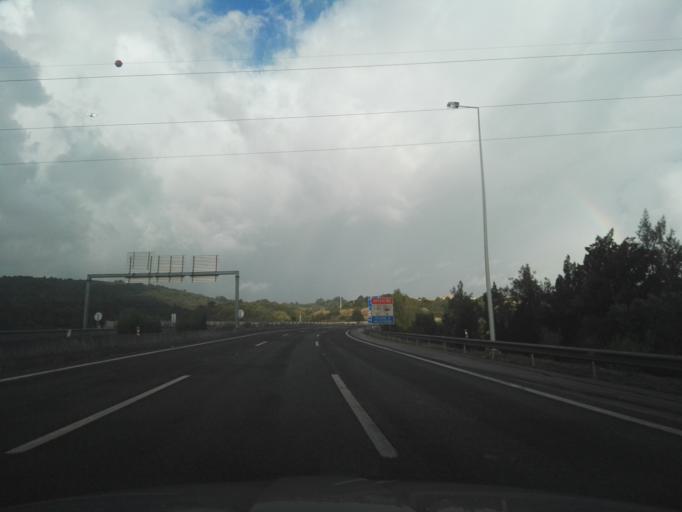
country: PT
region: Lisbon
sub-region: Vila Franca de Xira
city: Vialonga
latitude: 38.8960
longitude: -9.0522
